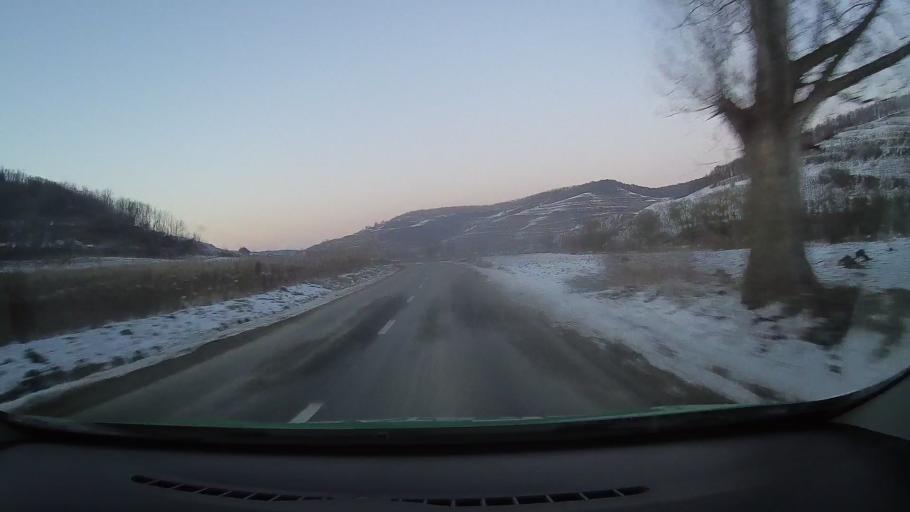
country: RO
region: Sibiu
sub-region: Comuna Atel
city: Atel
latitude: 46.1741
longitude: 24.4711
